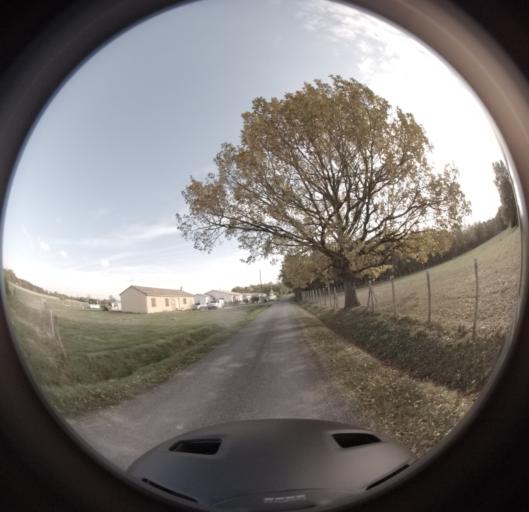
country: FR
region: Midi-Pyrenees
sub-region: Departement du Tarn-et-Garonne
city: Montbeton
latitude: 43.9952
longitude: 1.2834
